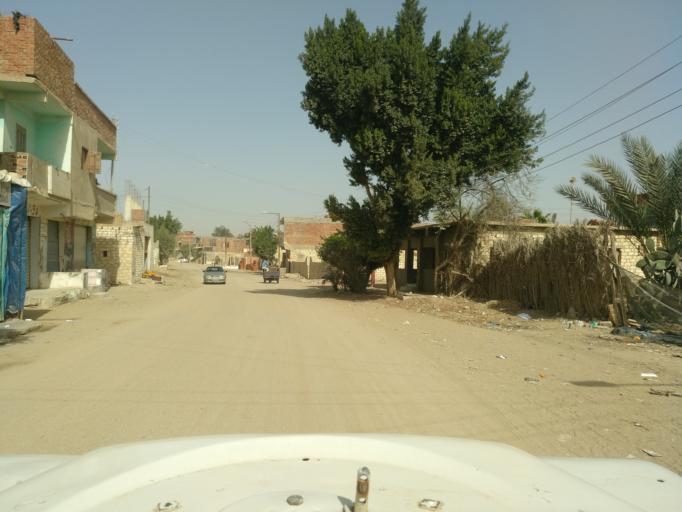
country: EG
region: Al Buhayrah
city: Beheira
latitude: 30.3804
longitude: 30.3451
